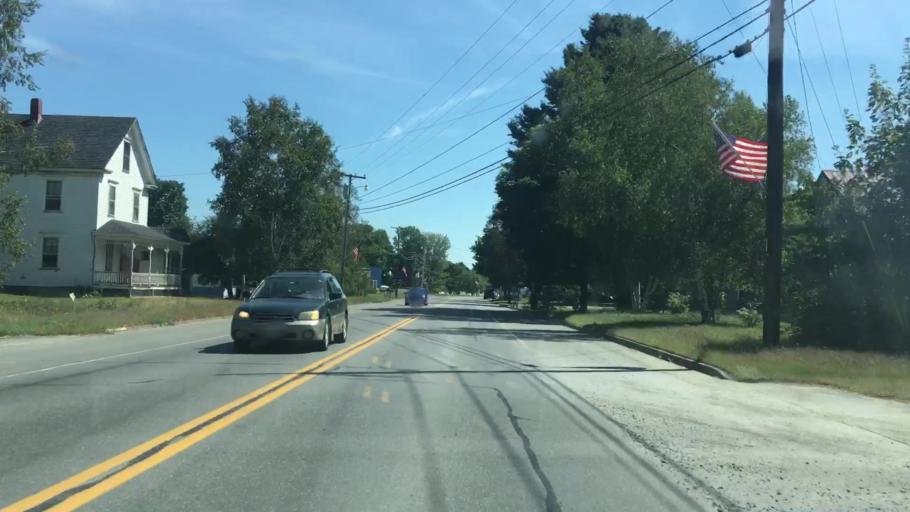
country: US
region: Maine
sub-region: Piscataquis County
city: Milo
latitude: 45.2626
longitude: -68.9902
